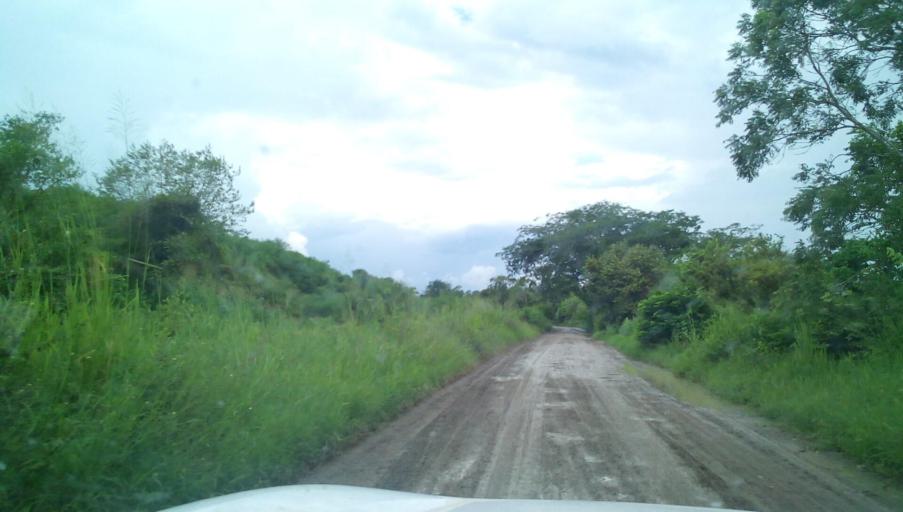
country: MX
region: Veracruz
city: Panuco
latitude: 21.8090
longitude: -98.1070
